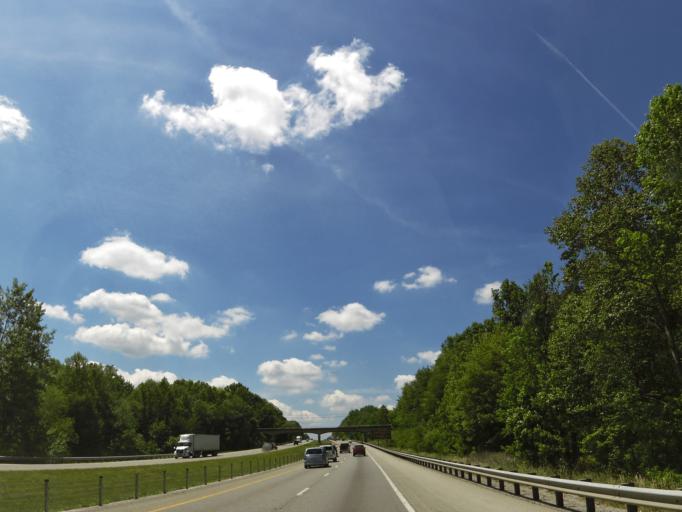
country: US
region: Kentucky
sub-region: Whitley County
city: Corbin
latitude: 36.9473
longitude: -84.1227
